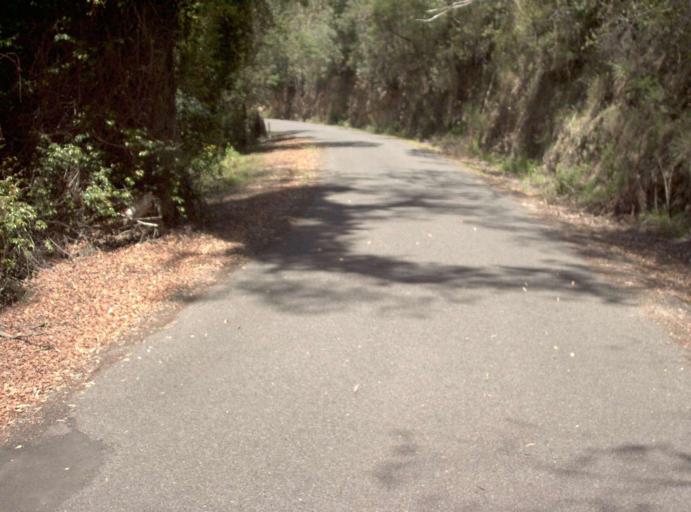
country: AU
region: New South Wales
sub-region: Bombala
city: Bombala
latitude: -37.4562
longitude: 148.9348
